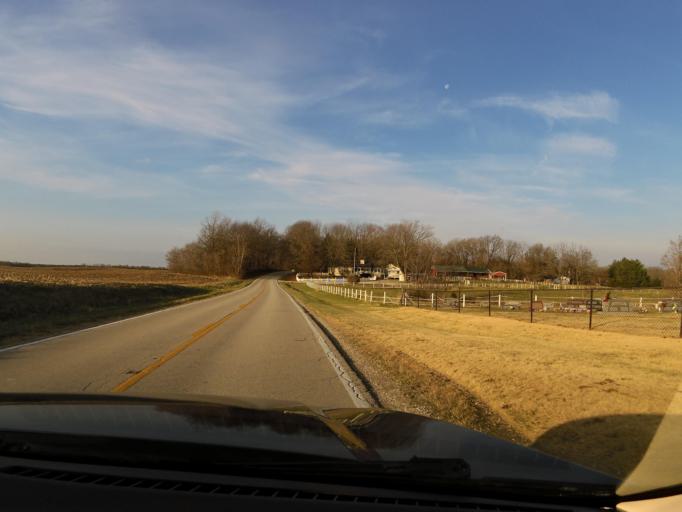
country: US
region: Illinois
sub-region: Fayette County
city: Vandalia
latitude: 38.9213
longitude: -89.2121
